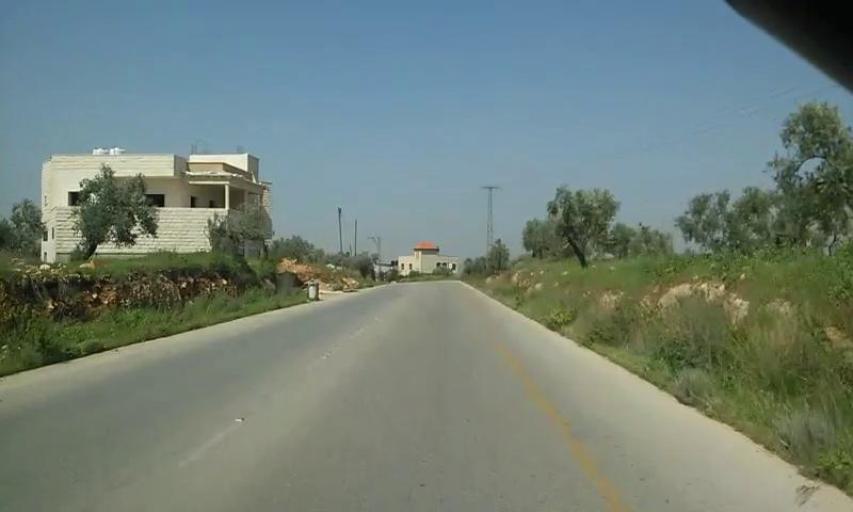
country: PS
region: West Bank
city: Az Zababidah
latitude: 32.3803
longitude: 35.3306
